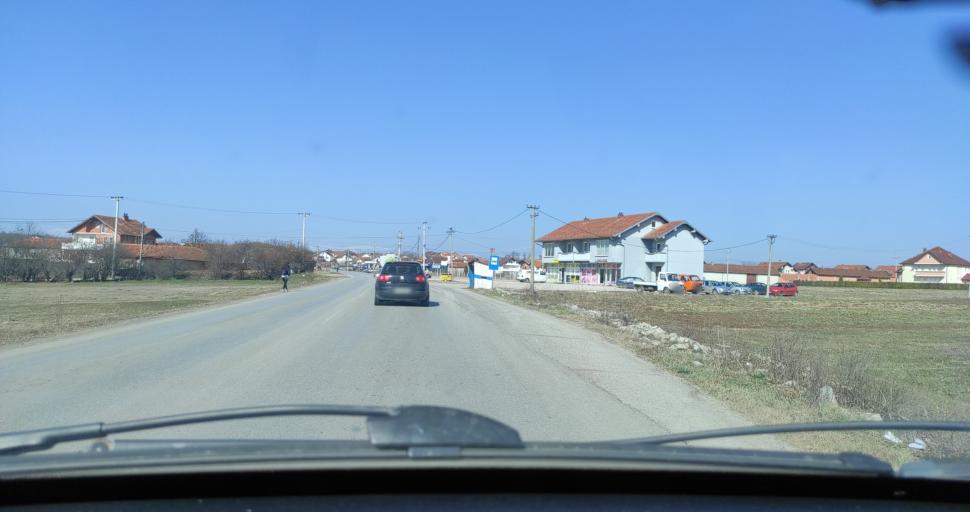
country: XK
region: Prizren
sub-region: Komuna e Malisheves
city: Llazice
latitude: 42.5825
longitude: 20.6935
